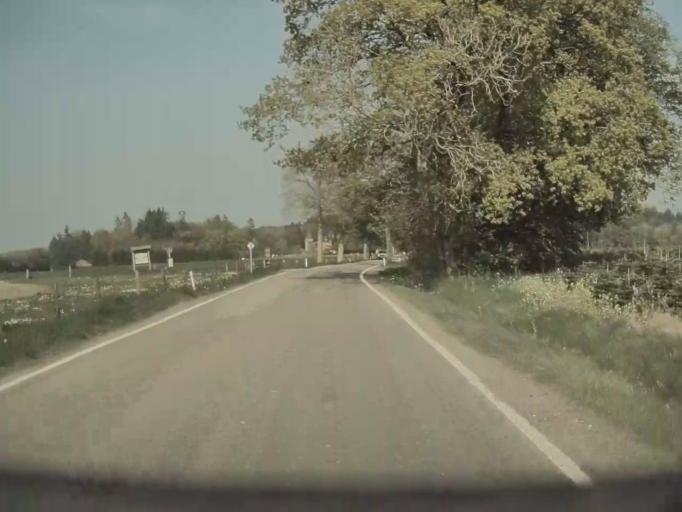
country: BE
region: Wallonia
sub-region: Province de Namur
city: Hamois
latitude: 50.2861
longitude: 5.1859
